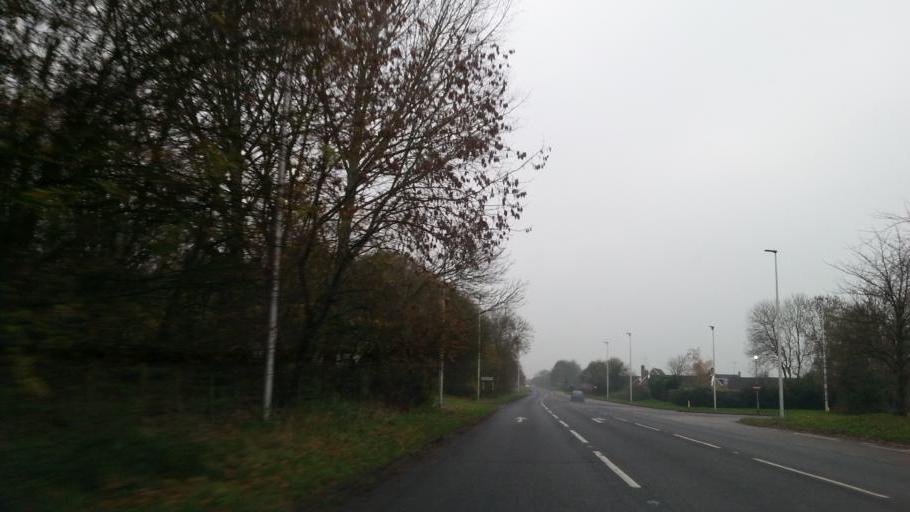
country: GB
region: England
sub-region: Peterborough
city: Castor
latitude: 52.5482
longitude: -0.3264
